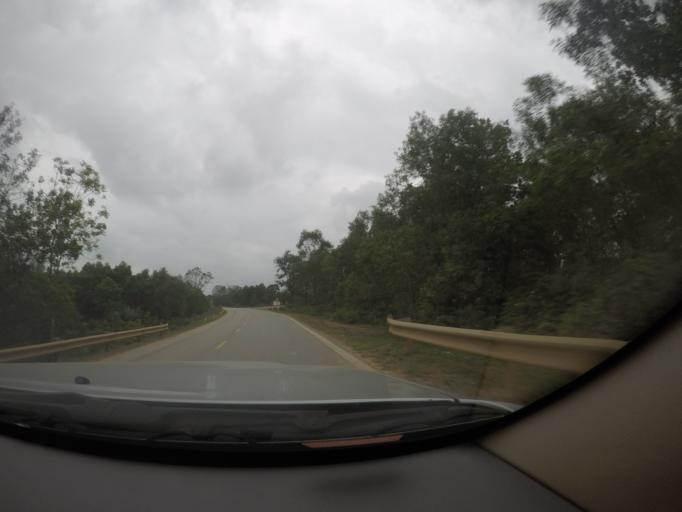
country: VN
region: Quang Tri
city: Cam Lo
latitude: 16.8402
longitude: 106.9979
